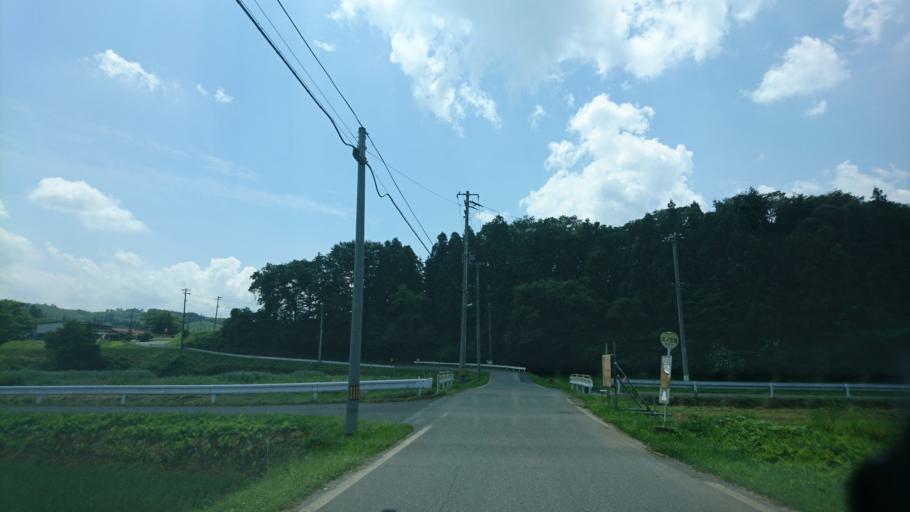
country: JP
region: Iwate
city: Ichinoseki
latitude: 38.9103
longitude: 141.2239
